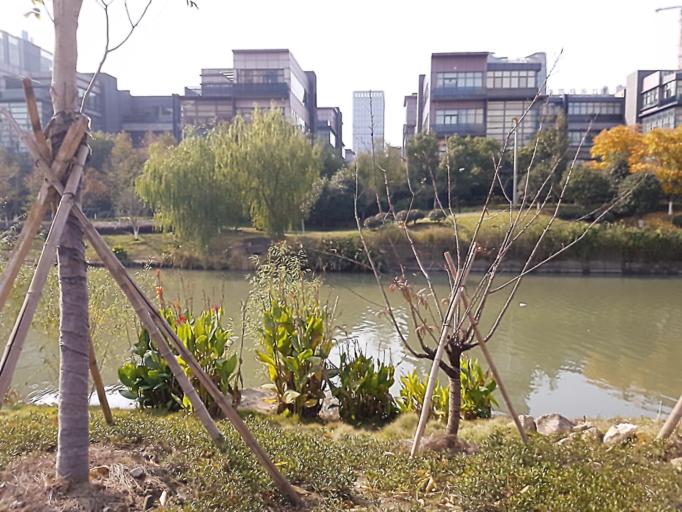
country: CN
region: Zhejiang Sheng
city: Cangqian
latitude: 30.2811
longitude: 120.0034
